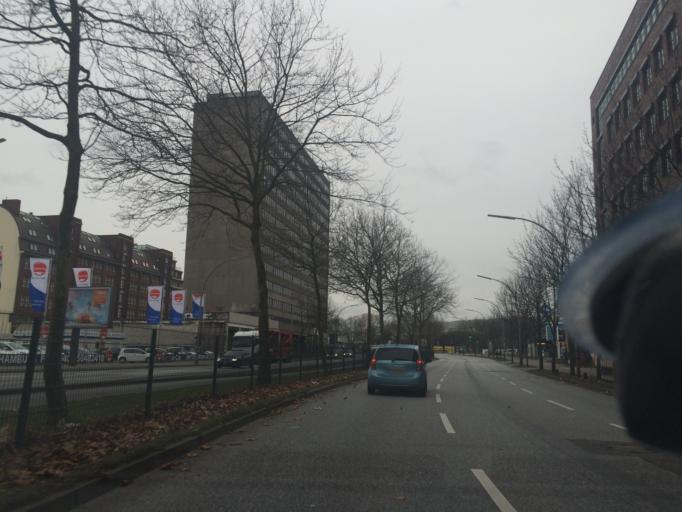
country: DE
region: Hamburg
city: Hamburg-Mitte
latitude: 53.5470
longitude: 10.0146
